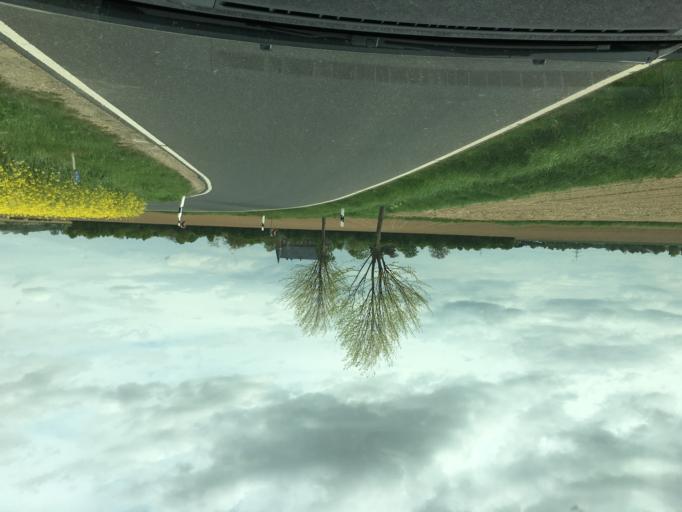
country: DE
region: North Rhine-Westphalia
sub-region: Regierungsbezirk Koln
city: Merzenich
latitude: 50.7871
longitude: 6.5477
